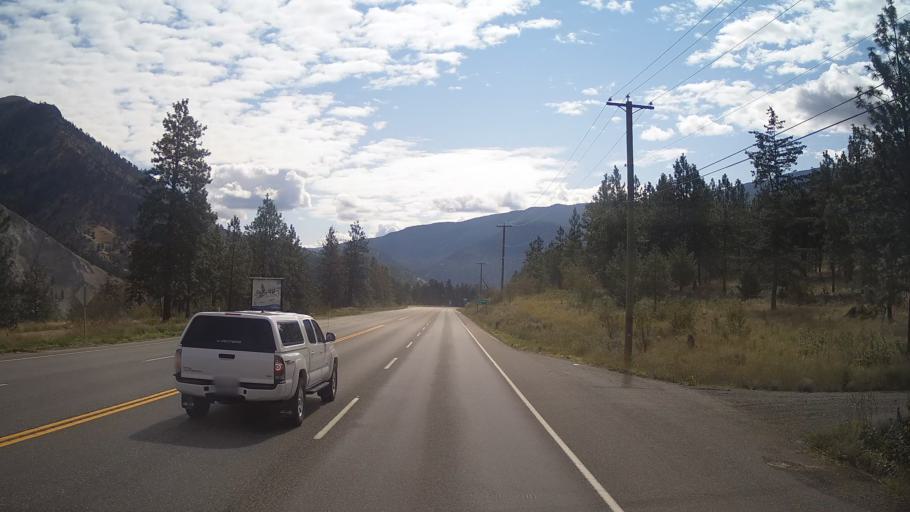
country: CA
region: British Columbia
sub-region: Thompson-Nicola Regional District
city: Ashcroft
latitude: 50.2592
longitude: -121.5338
